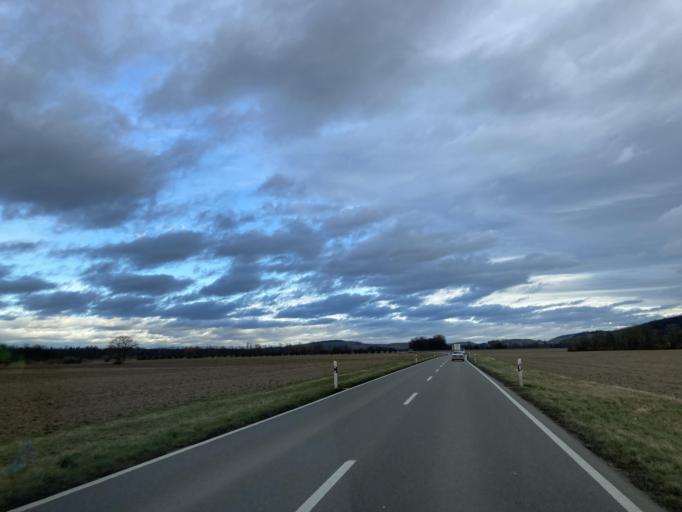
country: DE
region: Baden-Wuerttemberg
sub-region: Freiburg Region
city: Breisach am Rhein
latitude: 48.0557
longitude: 7.5927
